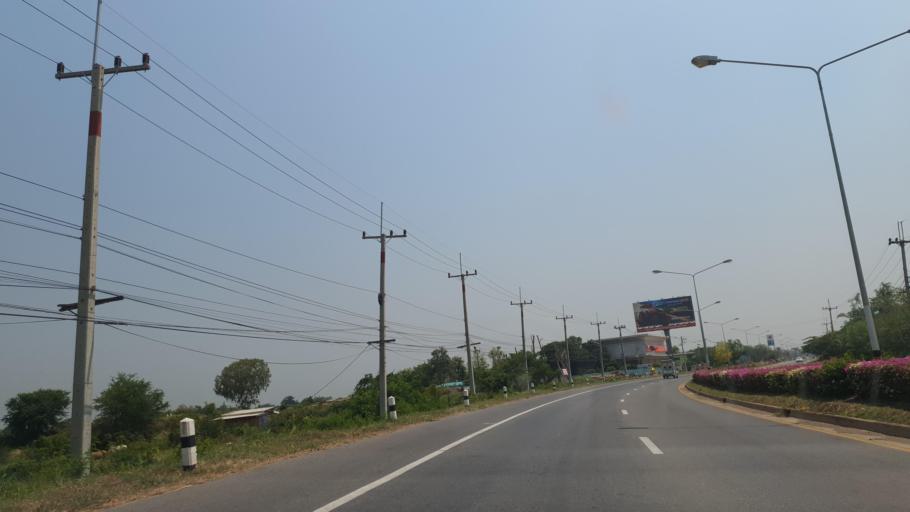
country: TH
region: Suphan Buri
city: U Thong
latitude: 14.2430
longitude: 99.8079
